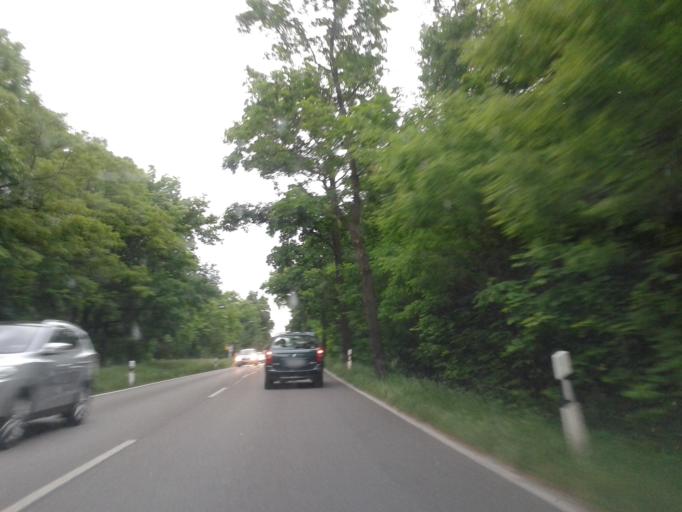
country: DE
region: Saxony
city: Radebeul
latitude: 51.1060
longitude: 13.7093
